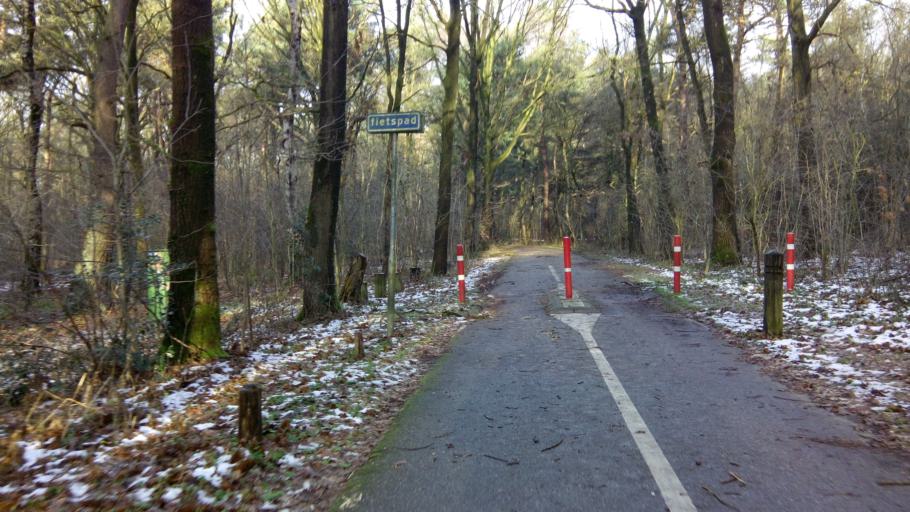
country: NL
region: North Brabant
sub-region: Gemeente Cuijk
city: Cuijk
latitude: 51.7845
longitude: 5.8676
